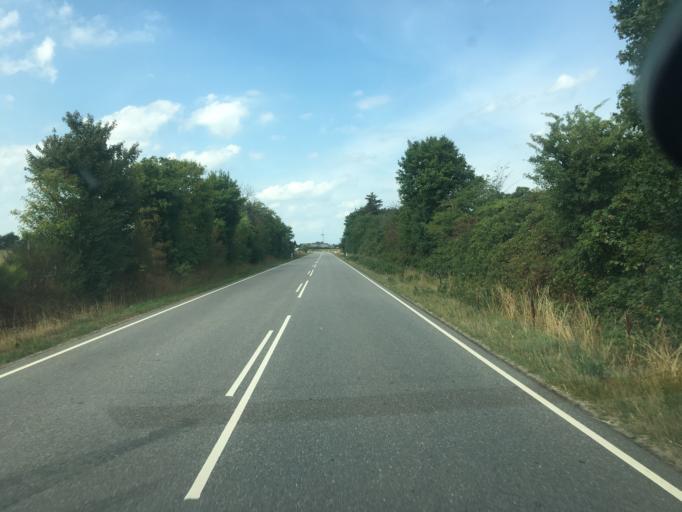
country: DK
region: South Denmark
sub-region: Aabenraa Kommune
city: Krusa
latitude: 54.9397
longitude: 9.3575
